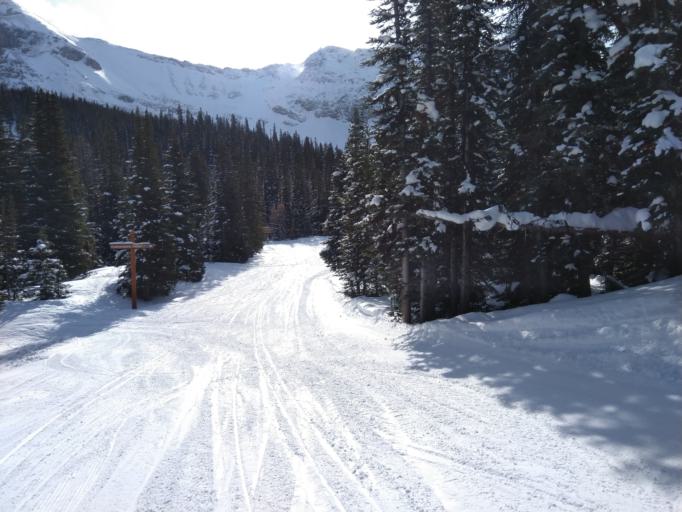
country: CA
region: Alberta
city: Banff
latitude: 51.0860
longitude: -115.7698
